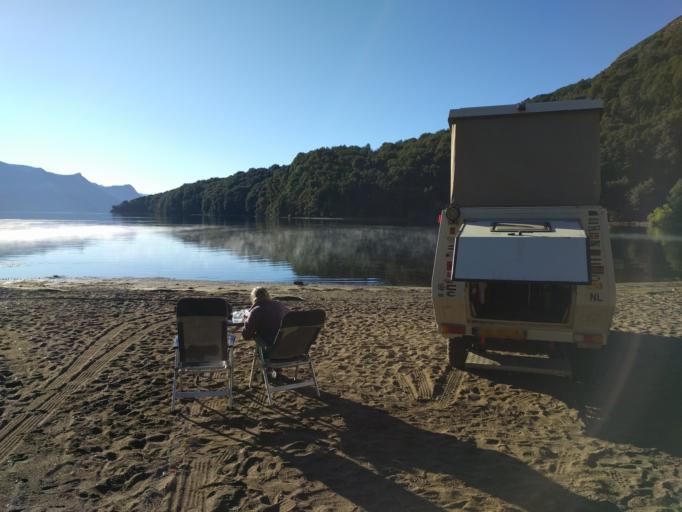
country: AR
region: Neuquen
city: Villa La Angostura
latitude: -40.6140
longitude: -71.5468
